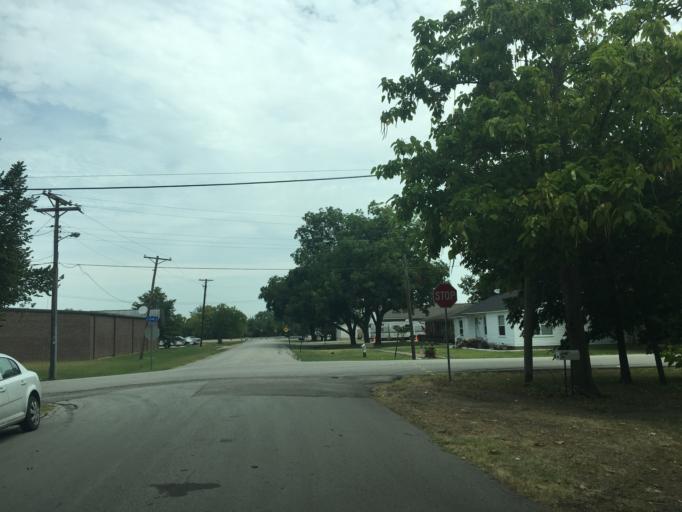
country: US
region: Texas
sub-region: Collin County
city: Wylie
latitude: 33.0137
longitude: -96.5344
